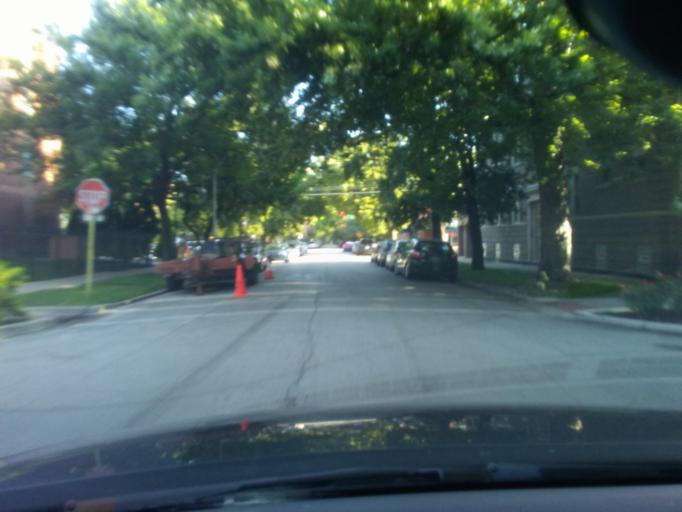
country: US
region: Illinois
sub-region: Cook County
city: Evanston
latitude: 41.9753
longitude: -87.6647
